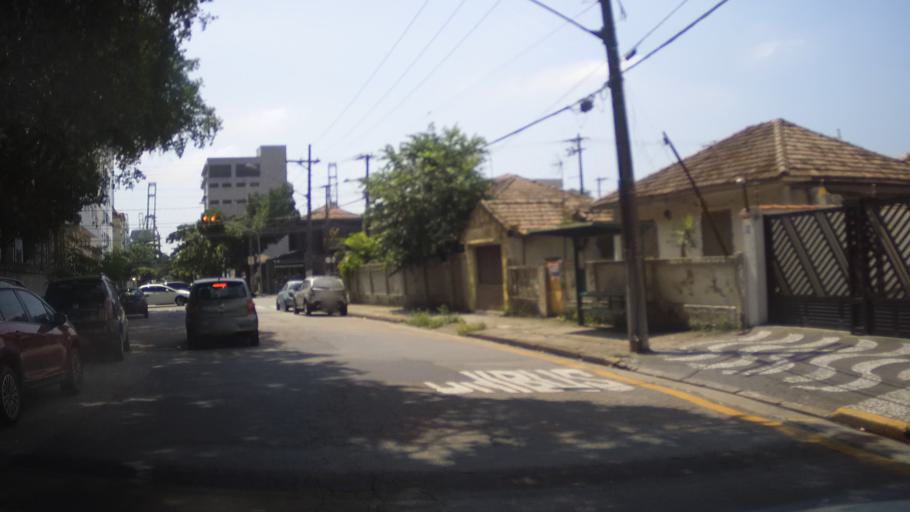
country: BR
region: Sao Paulo
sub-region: Santos
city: Santos
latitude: -23.9783
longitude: -46.2993
